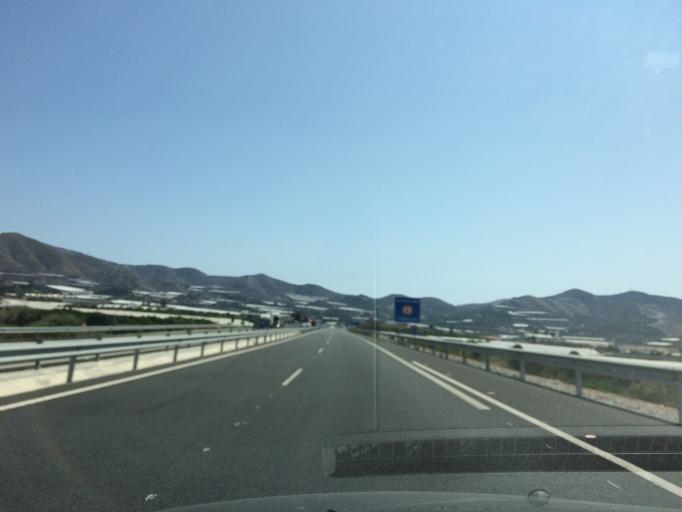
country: ES
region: Andalusia
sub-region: Provincia de Granada
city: Motril
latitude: 36.7354
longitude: -3.4820
